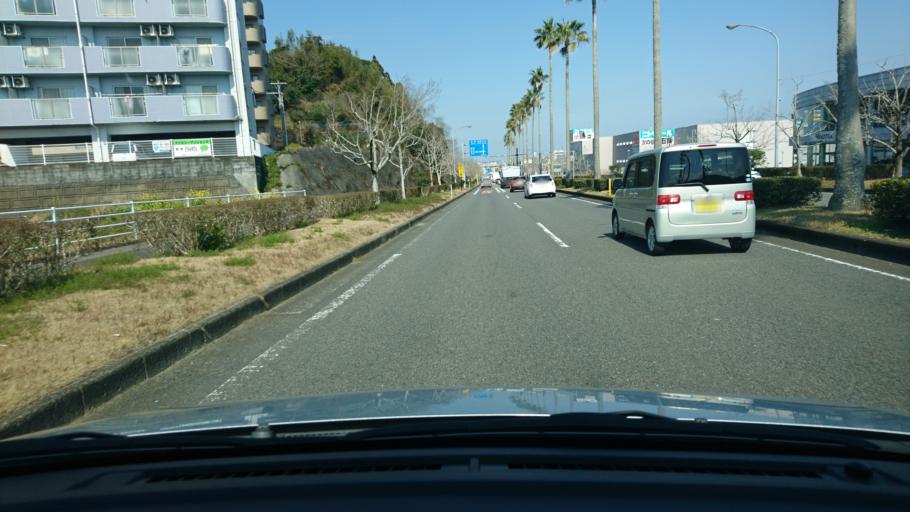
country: JP
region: Miyazaki
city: Miyazaki-shi
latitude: 31.8836
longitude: 131.4111
